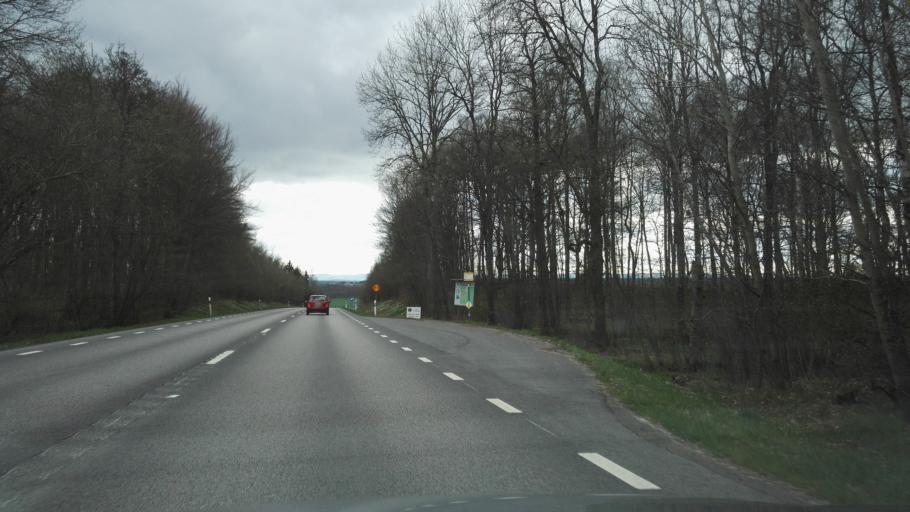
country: SE
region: Skane
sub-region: Sjobo Kommun
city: Sjoebo
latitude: 55.6585
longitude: 13.7054
